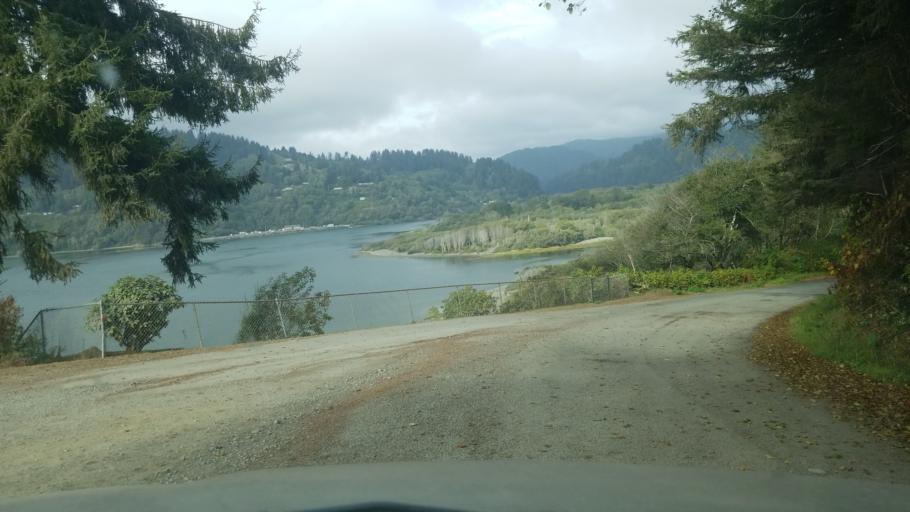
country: US
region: California
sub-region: Del Norte County
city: Bertsch-Oceanview
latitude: 41.5337
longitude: -124.0787
